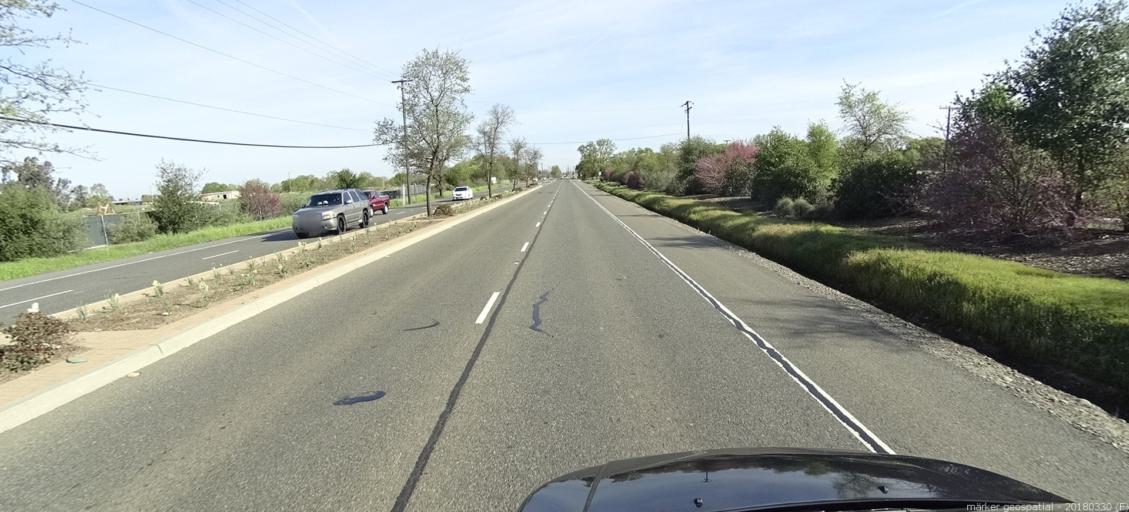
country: US
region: California
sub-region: Sacramento County
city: Rosemont
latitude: 38.5213
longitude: -121.3349
